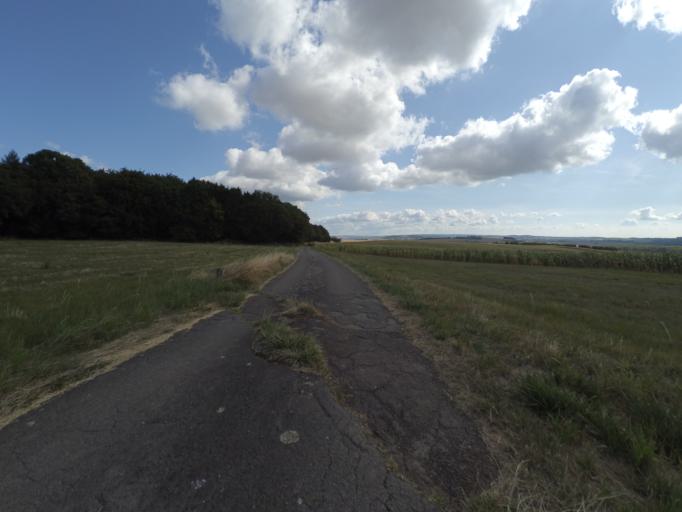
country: DE
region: Rheinland-Pfalz
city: Kirf
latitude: 49.5280
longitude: 6.4495
